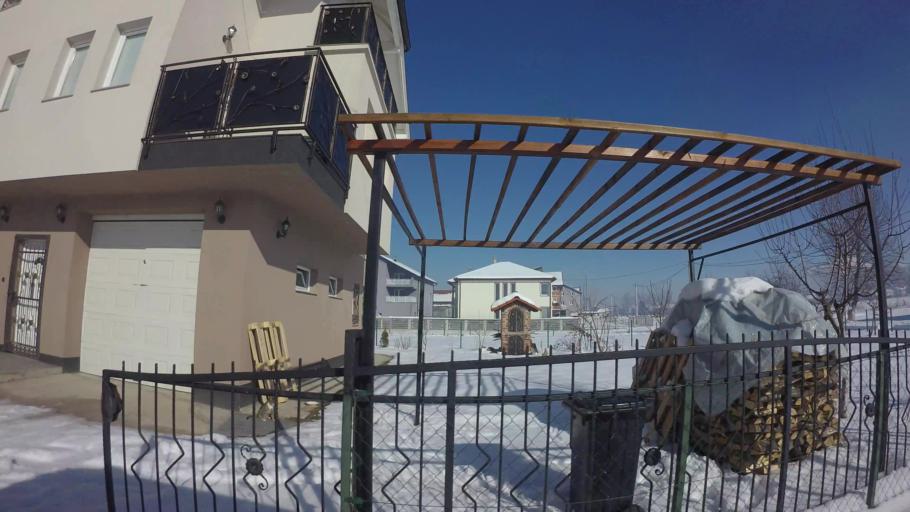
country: BA
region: Federation of Bosnia and Herzegovina
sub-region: Kanton Sarajevo
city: Sarajevo
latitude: 43.8128
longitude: 18.3068
